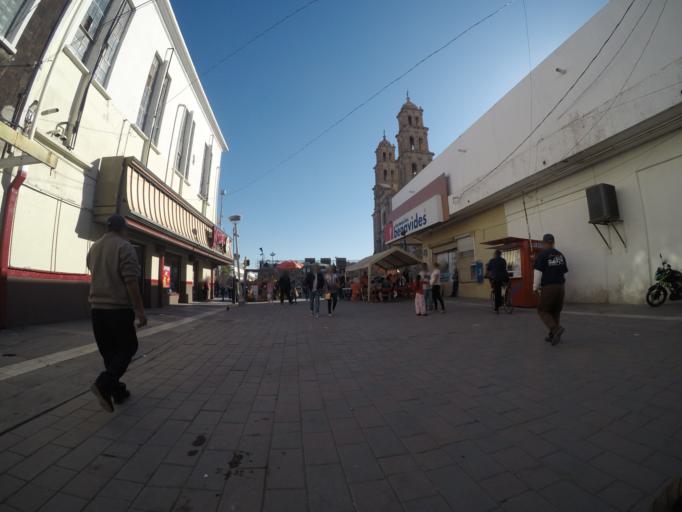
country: MX
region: Chihuahua
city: Ciudad Juarez
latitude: 31.7392
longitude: -106.4864
